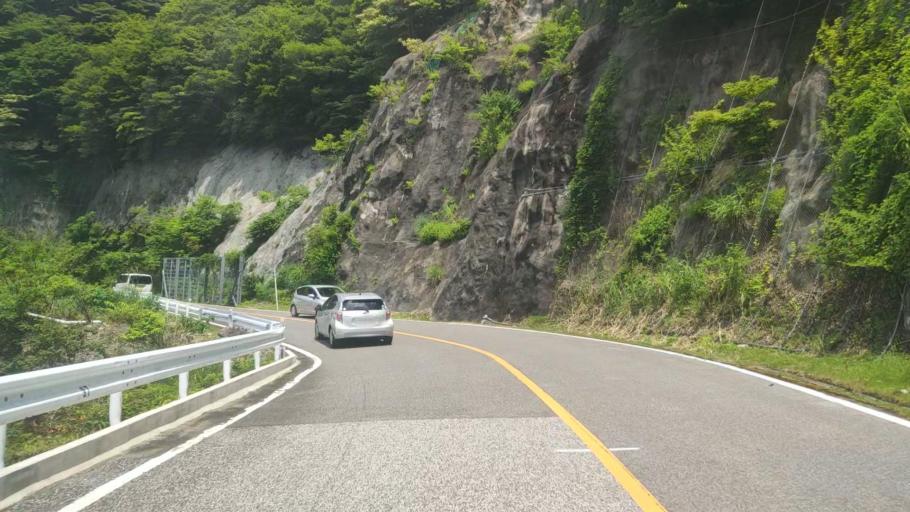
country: JP
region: Gifu
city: Tarui
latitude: 35.4009
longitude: 136.4264
